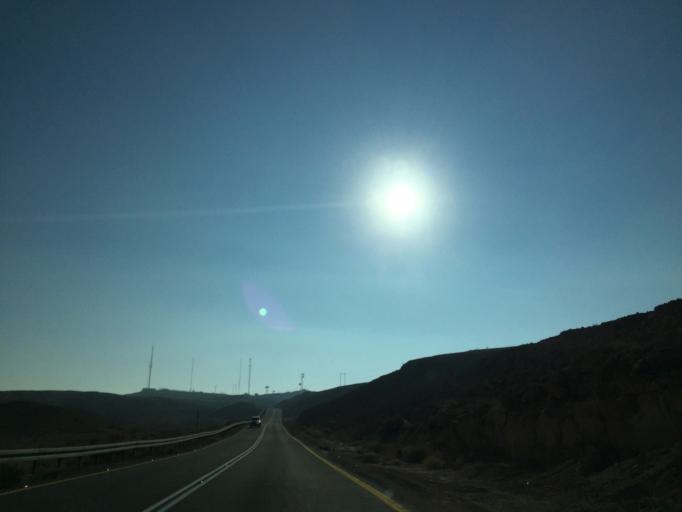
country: JO
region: Ma'an
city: Al Quwayrah
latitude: 30.0245
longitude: 35.0497
